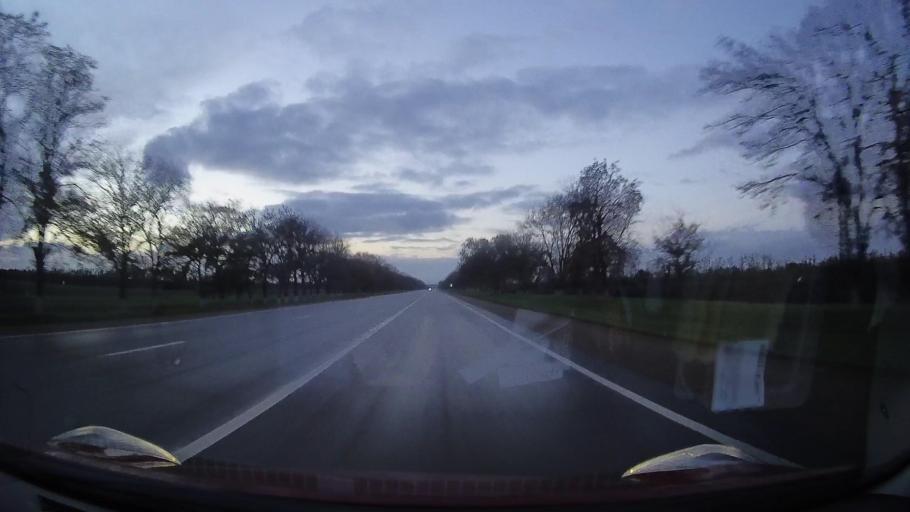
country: RU
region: Krasnodarskiy
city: Zavetnyy
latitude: 44.9005
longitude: 41.1856
